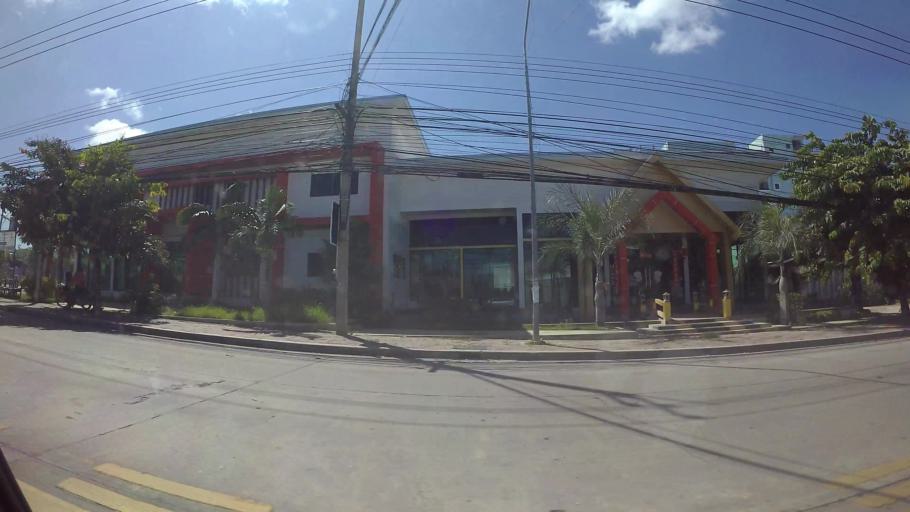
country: TH
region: Chon Buri
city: Phatthaya
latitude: 12.9443
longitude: 100.8956
